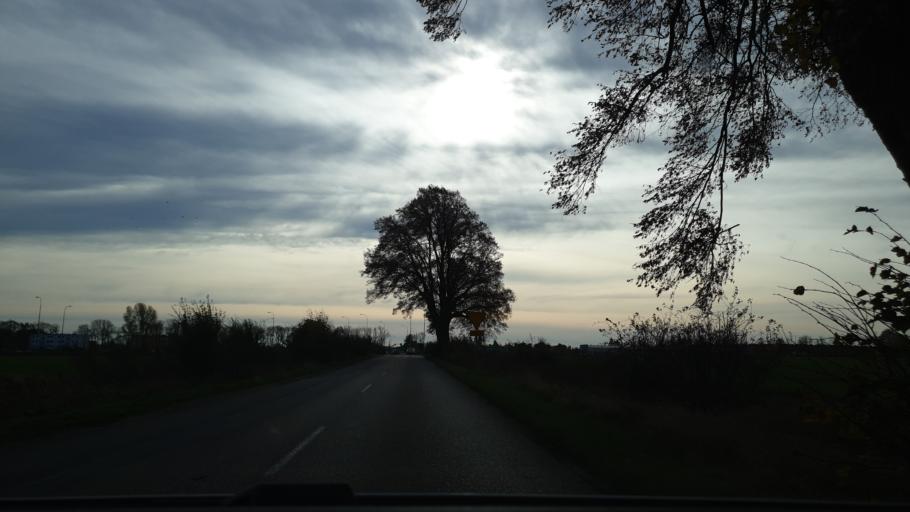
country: PL
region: Pomeranian Voivodeship
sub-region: Powiat pucki
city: Puck
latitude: 54.6898
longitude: 18.3671
